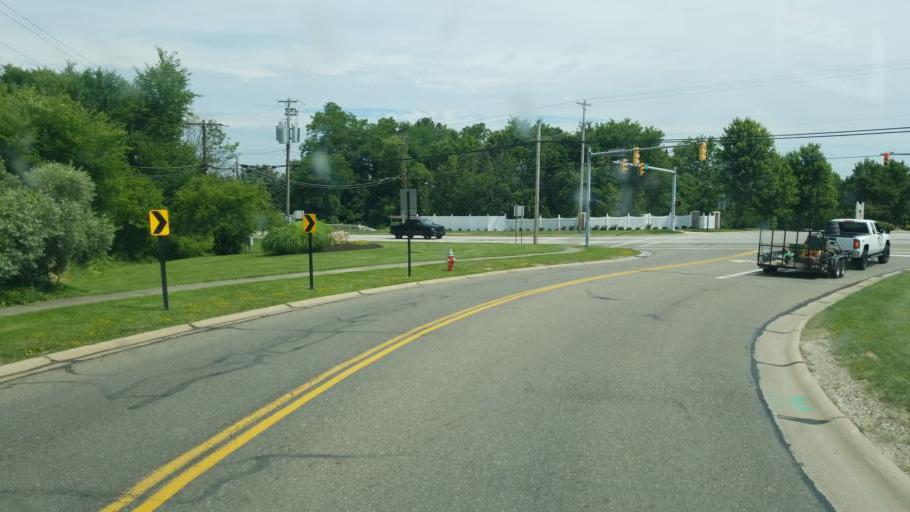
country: US
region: Ohio
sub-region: Cuyahoga County
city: Oakwood
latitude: 41.3406
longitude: -81.4789
